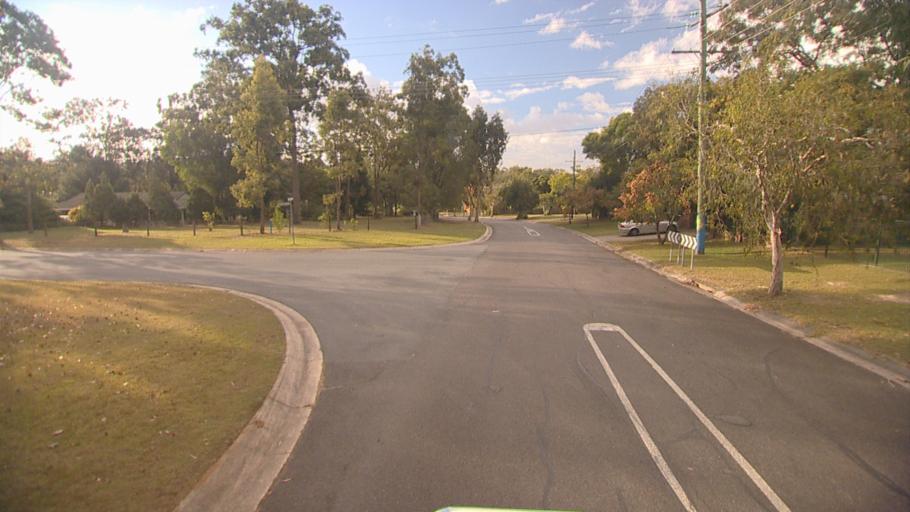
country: AU
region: Queensland
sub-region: Logan
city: Park Ridge South
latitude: -27.7050
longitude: 153.0206
